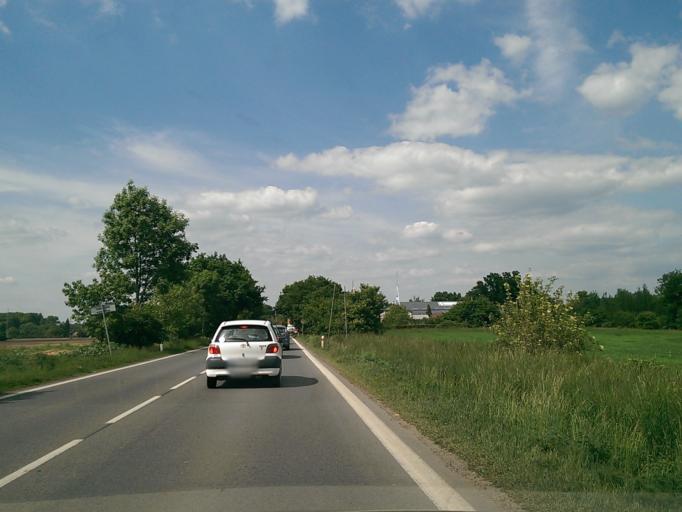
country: CZ
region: Central Bohemia
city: Libis
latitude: 50.2852
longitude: 14.4958
